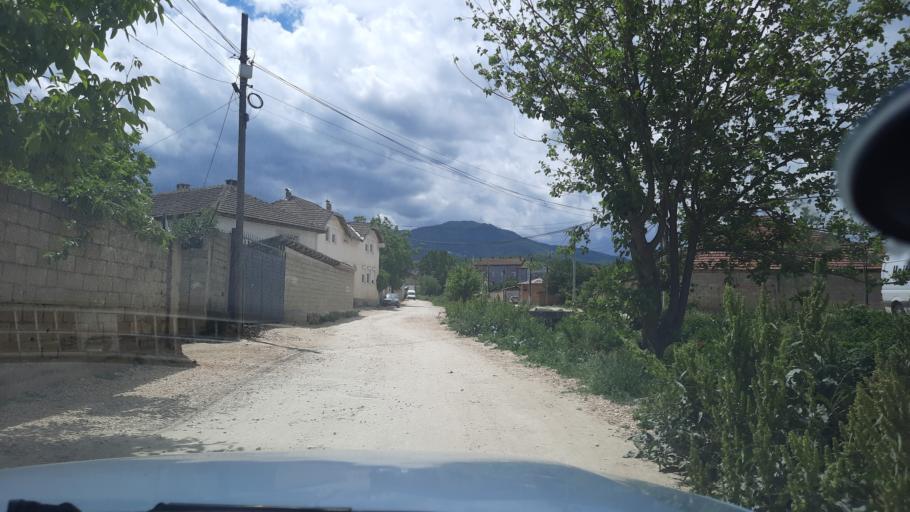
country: MK
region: Studenicani
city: Studenichani
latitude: 41.9227
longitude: 21.5362
